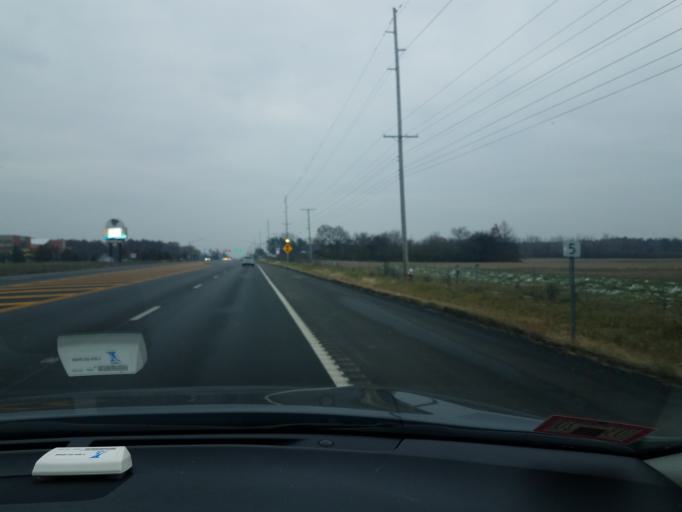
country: US
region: Ohio
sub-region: Erie County
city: Sandusky
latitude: 41.3859
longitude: -82.6475
